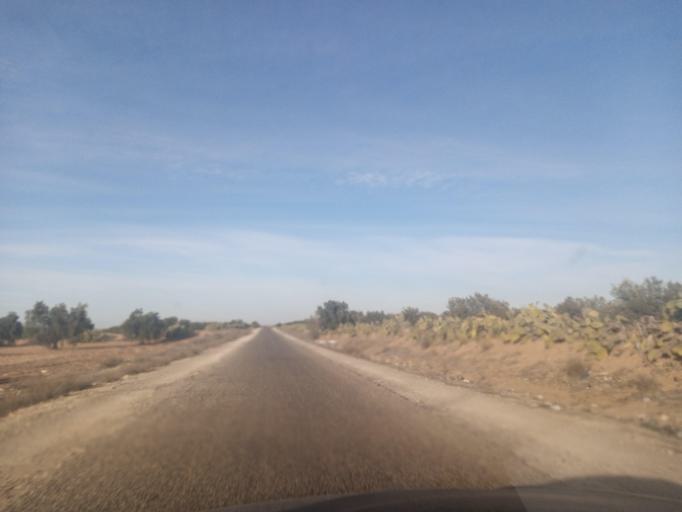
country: TN
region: Safaqis
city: Bi'r `Ali Bin Khalifah
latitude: 34.8479
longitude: 10.1604
